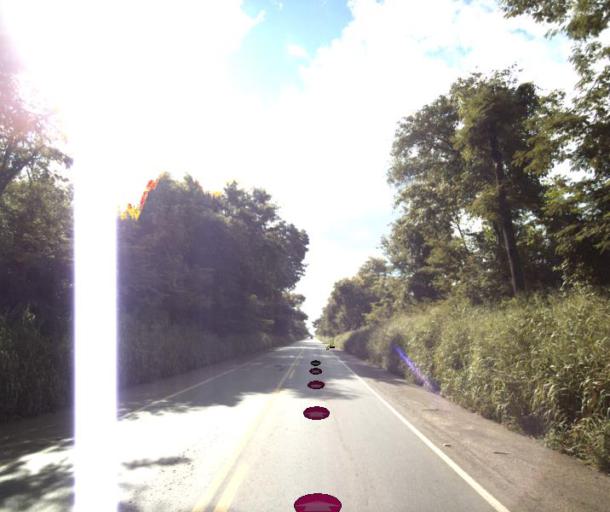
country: BR
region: Goias
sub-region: Jaragua
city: Jaragua
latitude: -15.7027
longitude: -49.3325
